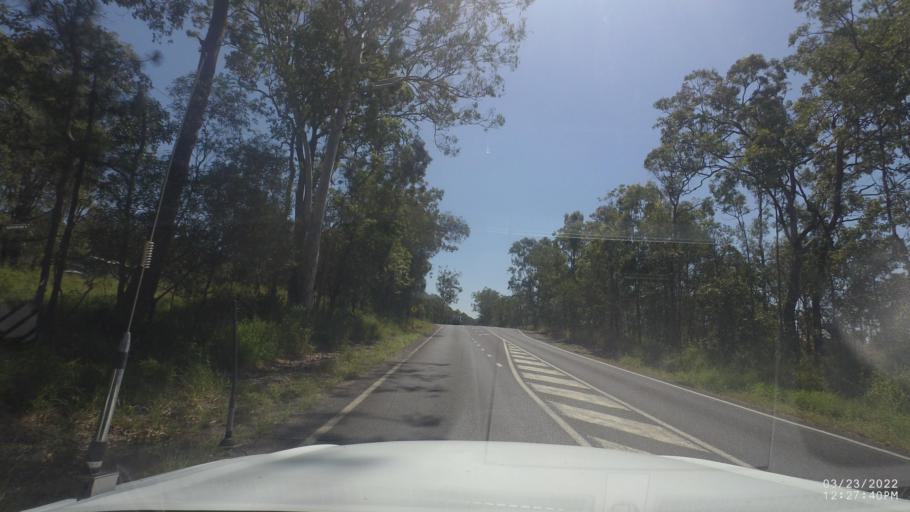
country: AU
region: Queensland
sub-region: Logan
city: Chambers Flat
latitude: -27.8227
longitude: 153.1016
